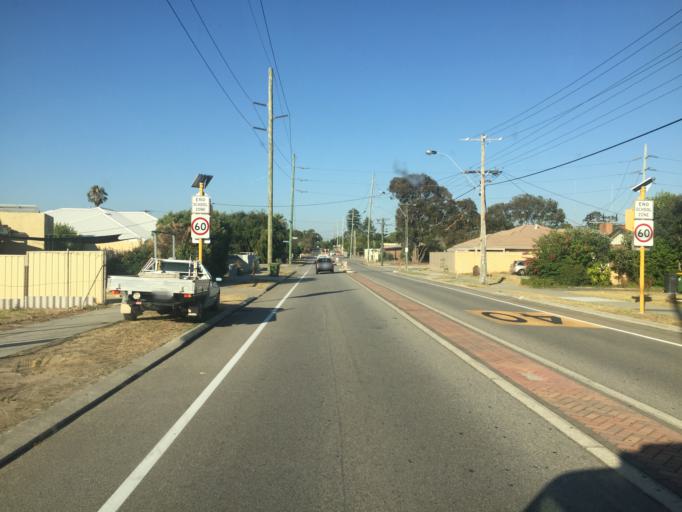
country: AU
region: Western Australia
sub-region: Belmont
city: Belmont
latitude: -31.9562
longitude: 115.9340
